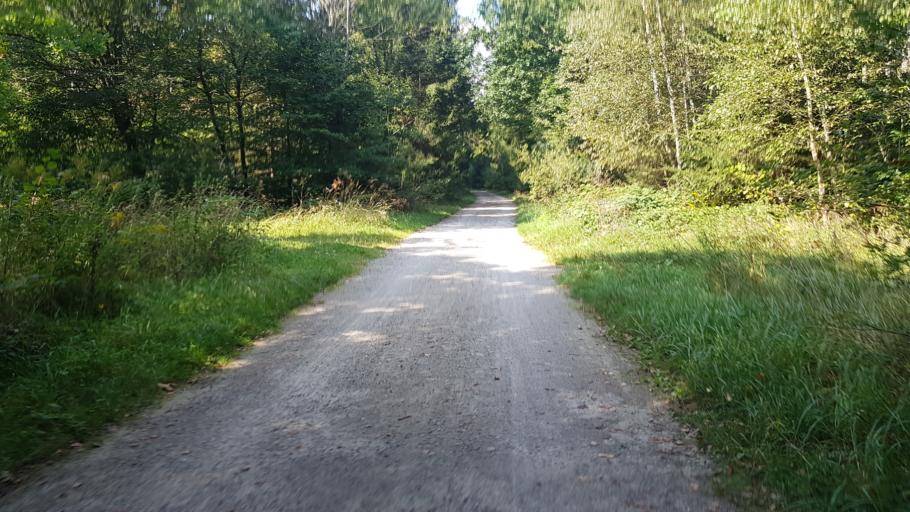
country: DE
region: Bavaria
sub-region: Upper Bavaria
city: Gauting
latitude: 48.0904
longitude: 11.3646
